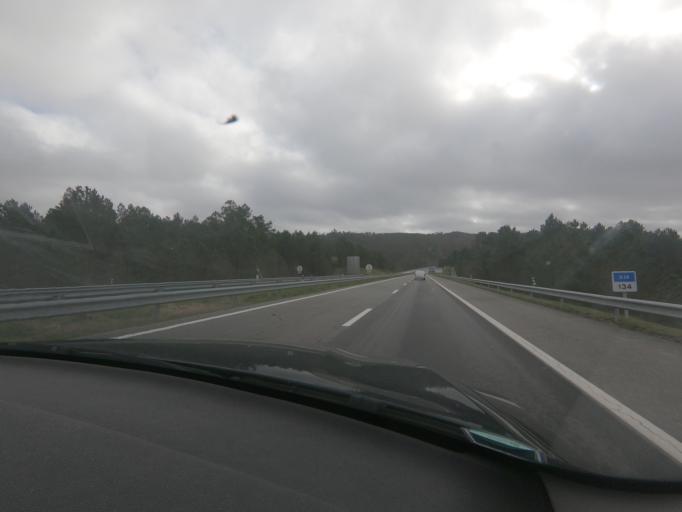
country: PT
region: Viseu
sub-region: Castro Daire
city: Castro Daire
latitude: 40.8474
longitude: -7.9272
